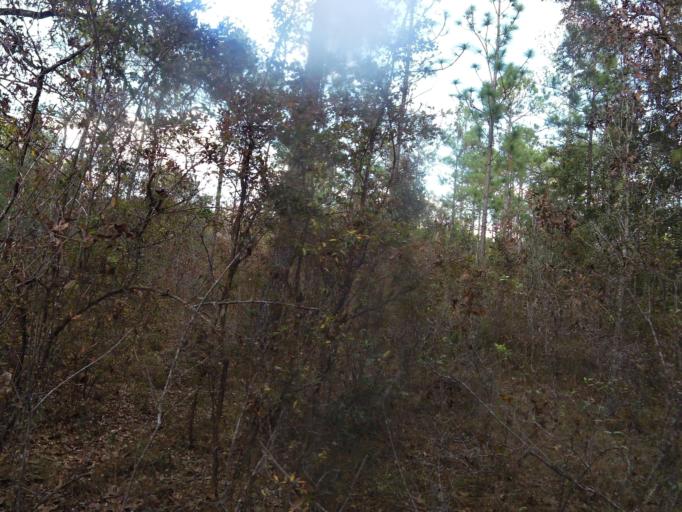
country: US
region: Florida
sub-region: Clay County
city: Middleburg
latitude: 30.1522
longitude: -81.9619
